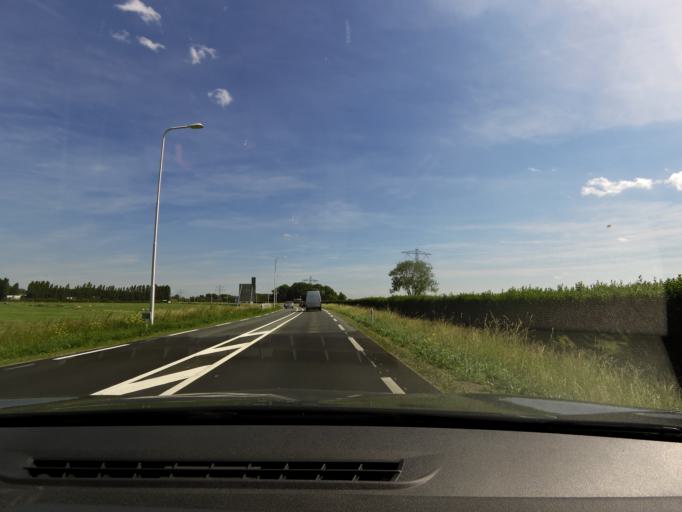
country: NL
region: South Holland
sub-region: Gemeente Maassluis
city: Maassluis
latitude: 51.8641
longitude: 4.2286
